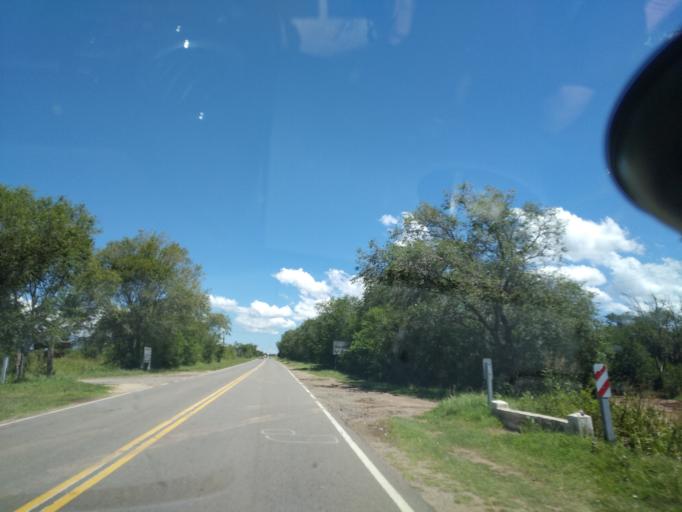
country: AR
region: Cordoba
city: Villa Cura Brochero
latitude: -31.5833
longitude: -65.1118
